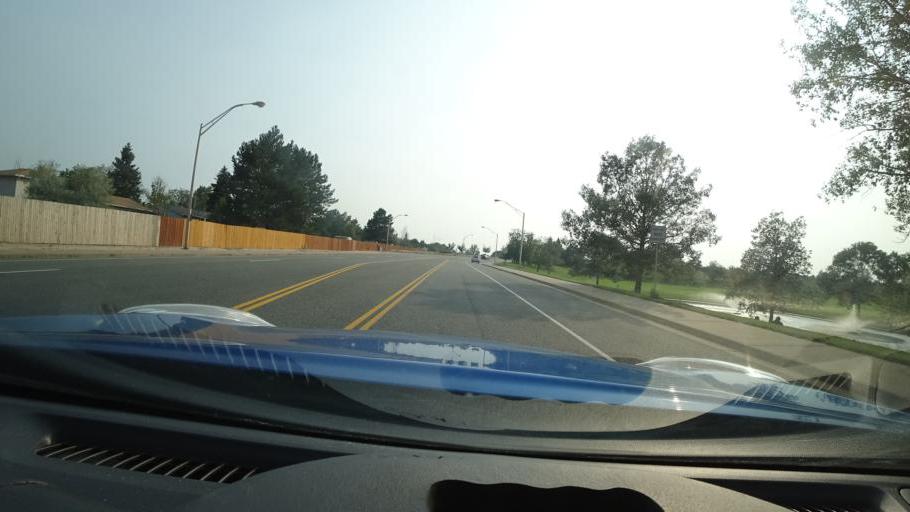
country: US
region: Colorado
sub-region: Adams County
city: Aurora
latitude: 39.6668
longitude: -104.8078
